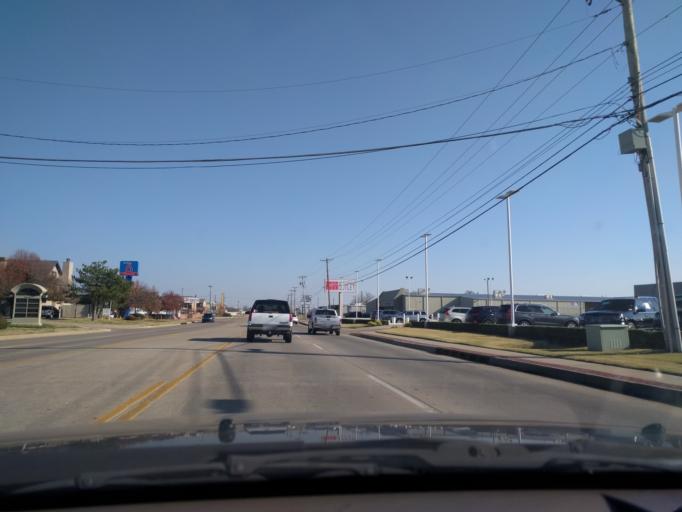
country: US
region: Oklahoma
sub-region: Tulsa County
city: Broken Arrow
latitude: 36.1044
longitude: -95.8851
